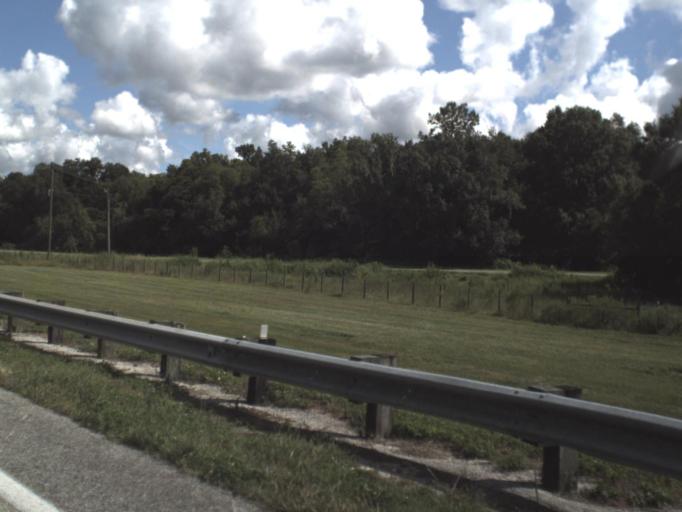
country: US
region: Florida
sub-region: Pasco County
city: Zephyrhills North
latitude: 28.3022
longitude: -82.0558
